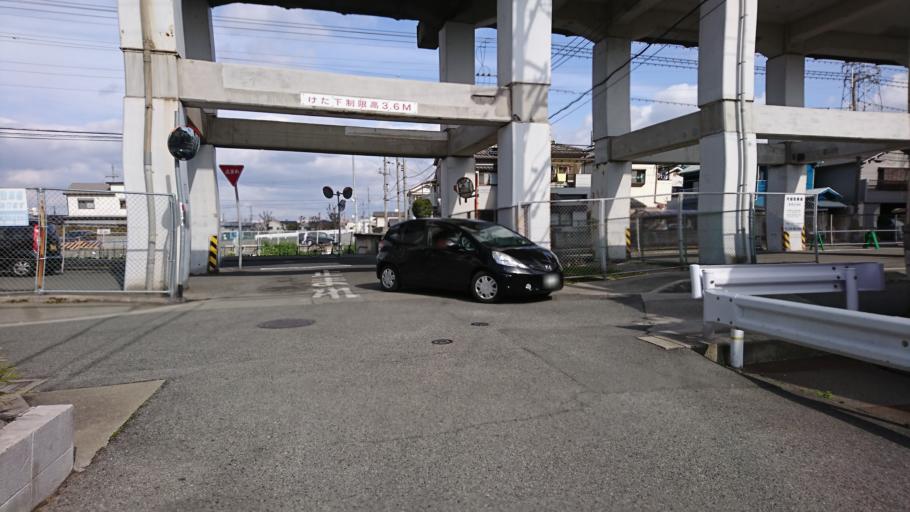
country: JP
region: Hyogo
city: Kakogawacho-honmachi
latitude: 34.7386
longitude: 134.8388
